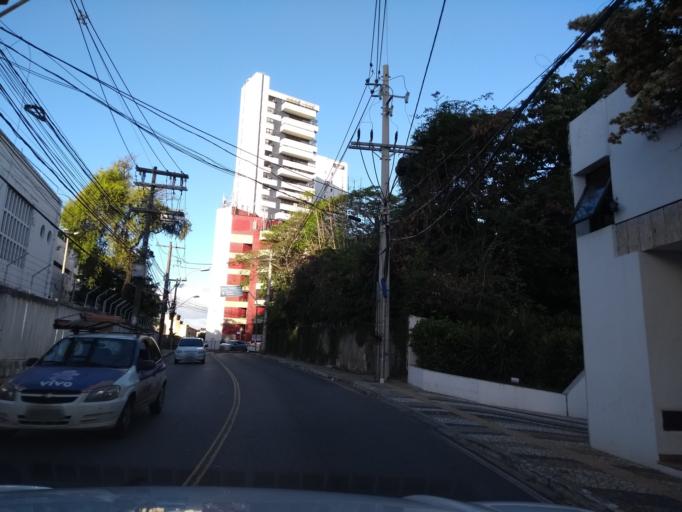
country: BR
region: Bahia
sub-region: Salvador
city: Salvador
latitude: -12.9966
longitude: -38.4879
